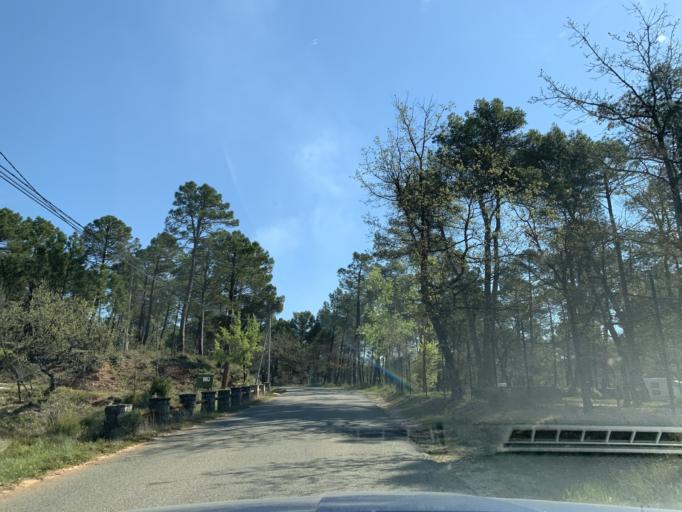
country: FR
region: Provence-Alpes-Cote d'Azur
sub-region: Departement du Vaucluse
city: Roussillon
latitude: 43.8909
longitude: 5.2773
